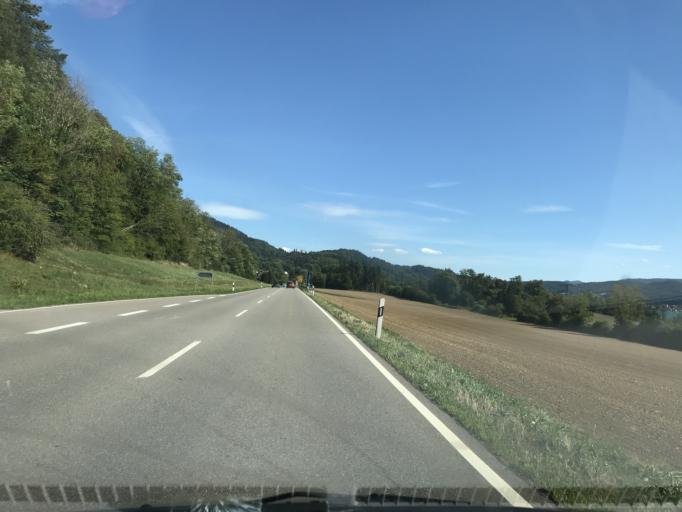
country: DE
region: Baden-Wuerttemberg
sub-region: Freiburg Region
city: Schworstadt
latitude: 47.5882
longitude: 7.8986
